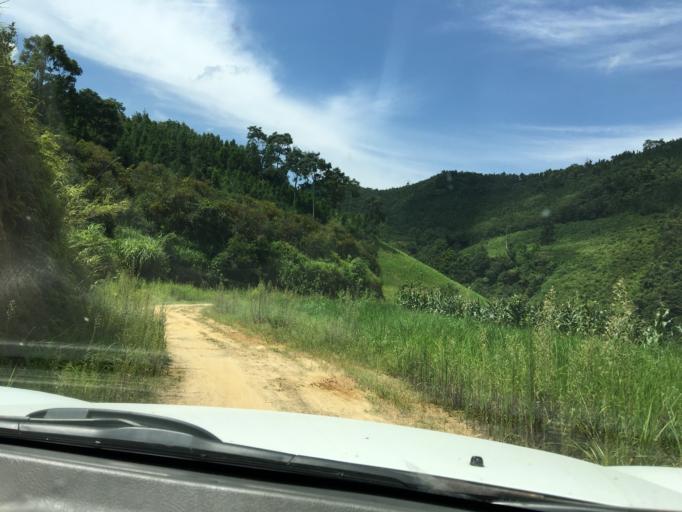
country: CN
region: Guangxi Zhuangzu Zizhiqu
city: Tongle
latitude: 24.9704
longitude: 105.9843
